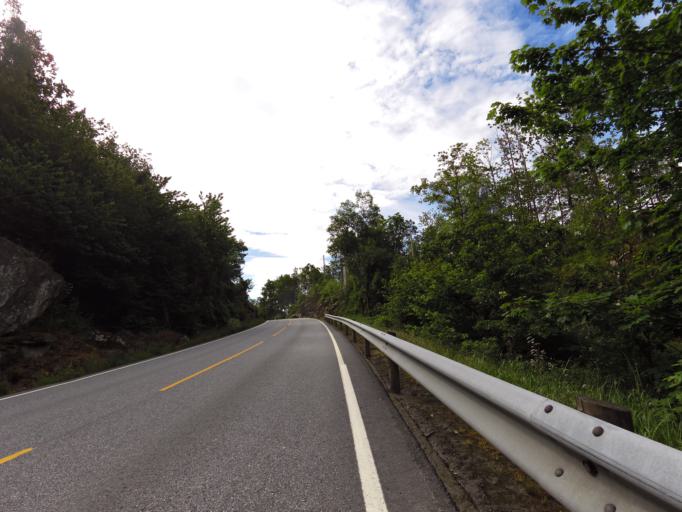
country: NO
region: Vest-Agder
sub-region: Lindesnes
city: Vigeland
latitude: 58.0545
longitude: 7.1819
